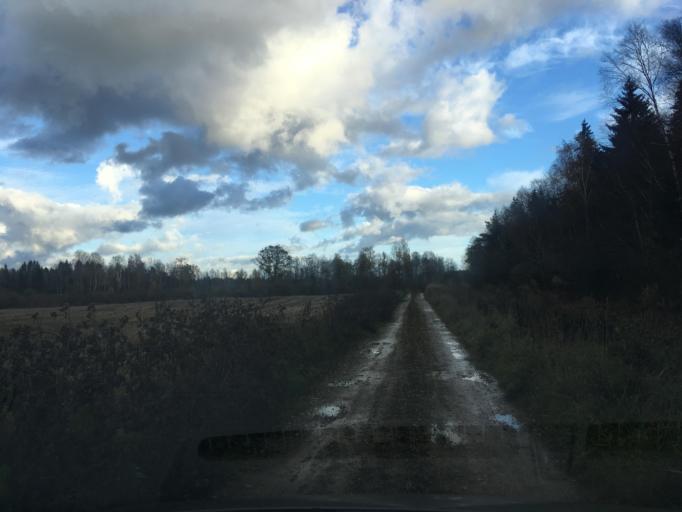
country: EE
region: Harju
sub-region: Raasiku vald
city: Arukula
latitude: 59.3578
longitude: 25.1051
